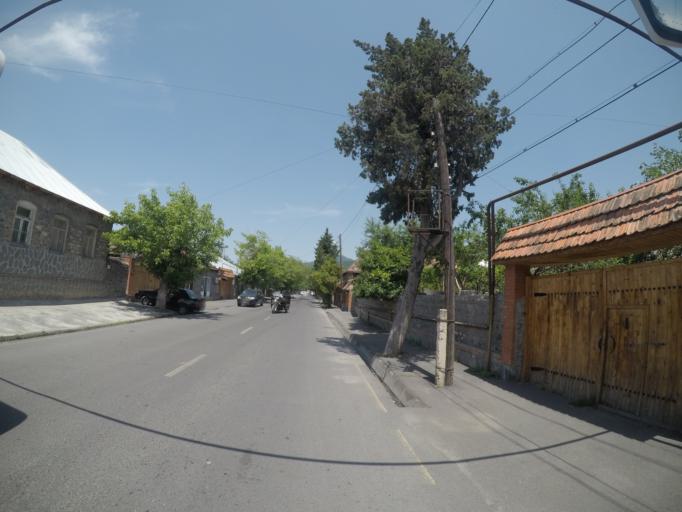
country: AZ
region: Qakh Rayon
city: Qax
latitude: 41.4171
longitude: 46.9195
